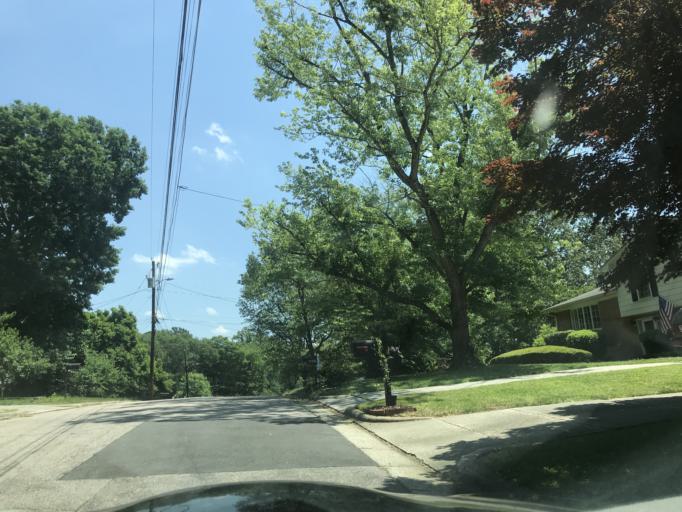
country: US
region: North Carolina
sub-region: Wake County
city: West Raleigh
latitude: 35.8445
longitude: -78.6337
